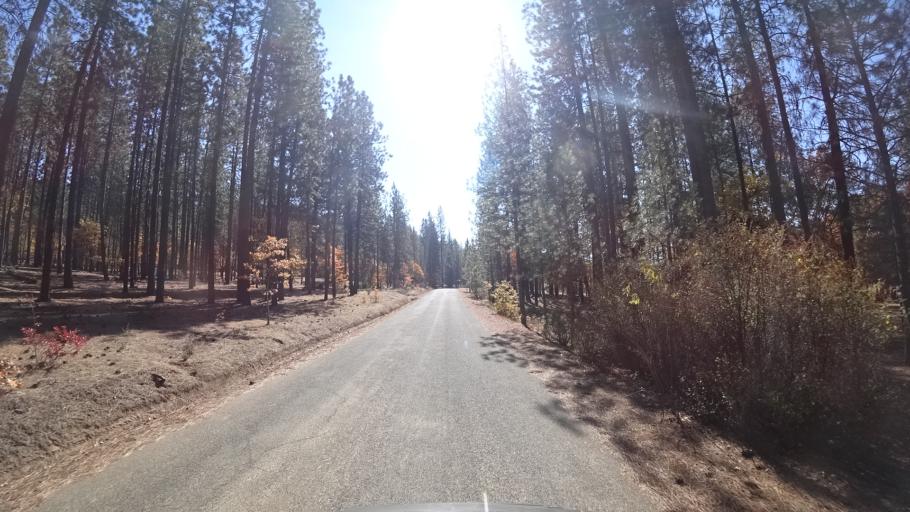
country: US
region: California
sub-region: Siskiyou County
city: Yreka
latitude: 41.6377
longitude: -122.8879
